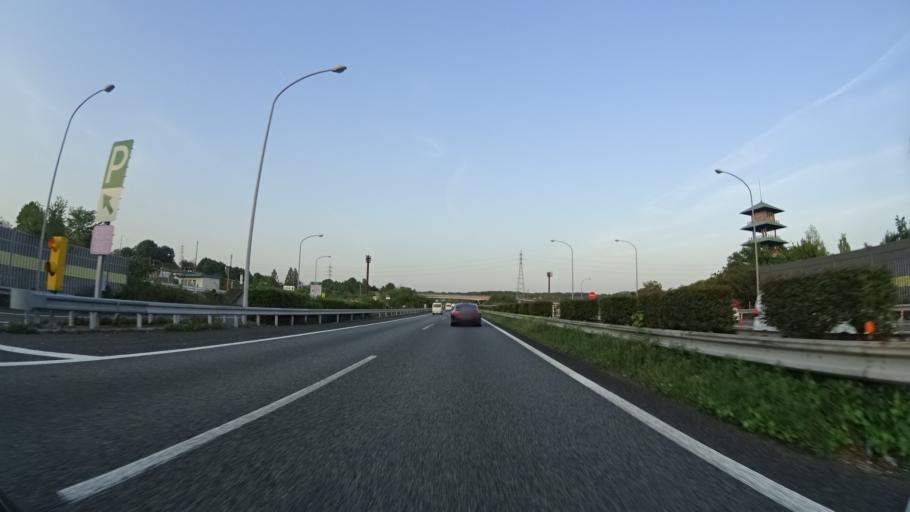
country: JP
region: Okayama
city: Okayama-shi
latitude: 34.6934
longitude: 133.8702
